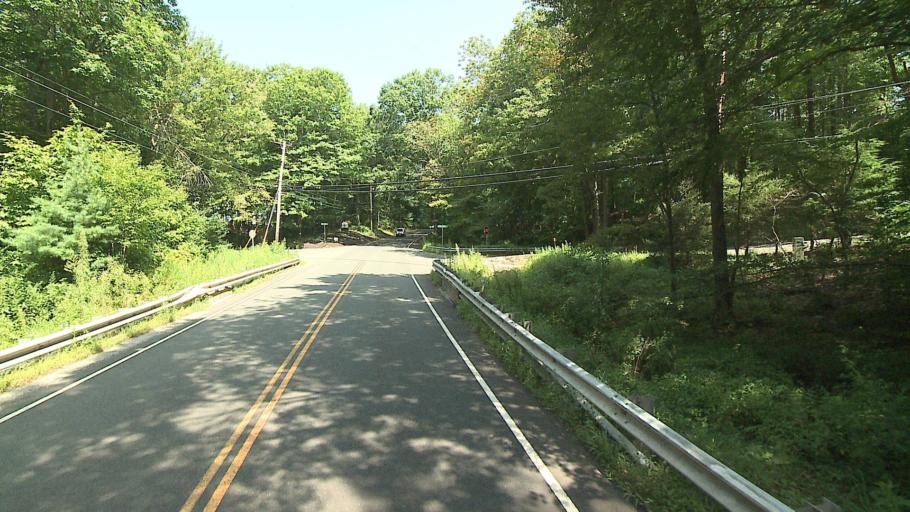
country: US
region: Connecticut
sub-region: Fairfield County
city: Trumbull
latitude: 41.2850
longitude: -73.2945
